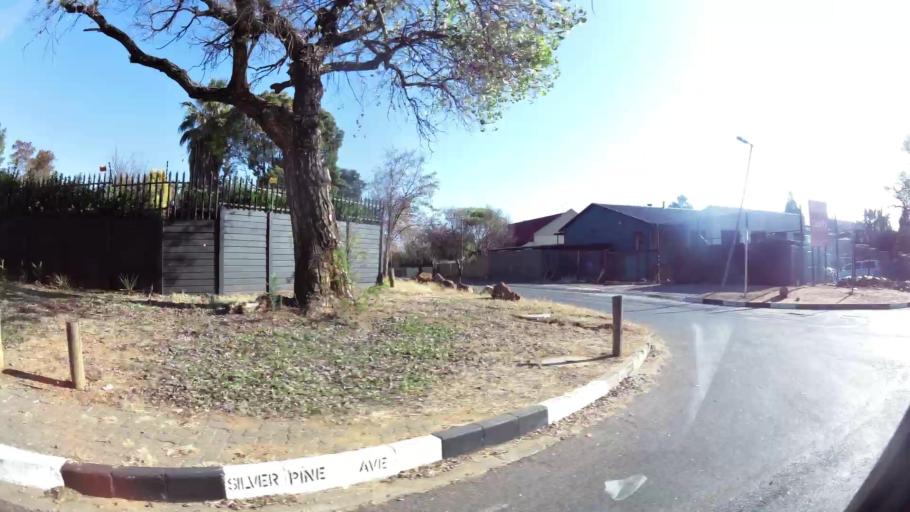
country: ZA
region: Gauteng
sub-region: City of Johannesburg Metropolitan Municipality
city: Roodepoort
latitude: -26.0921
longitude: 27.9724
